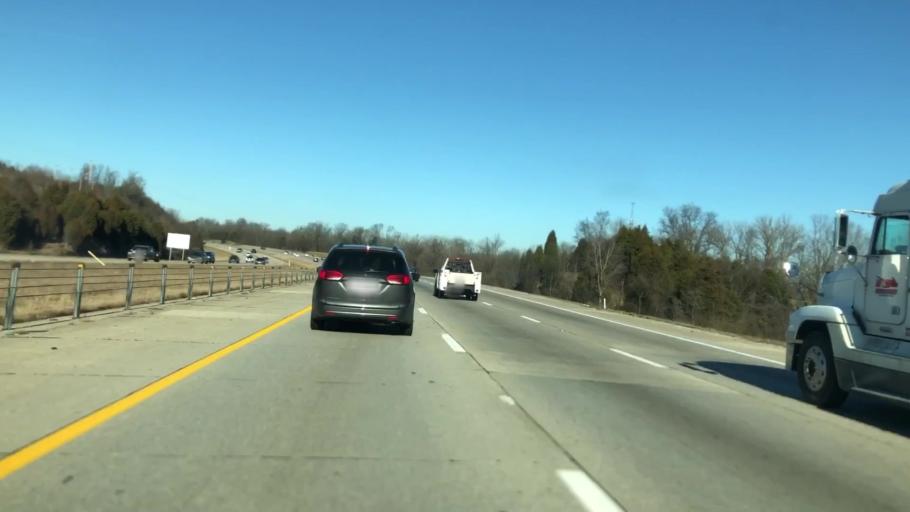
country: US
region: Kentucky
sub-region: Bullitt County
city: Shepherdsville
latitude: 38.0078
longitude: -85.6993
